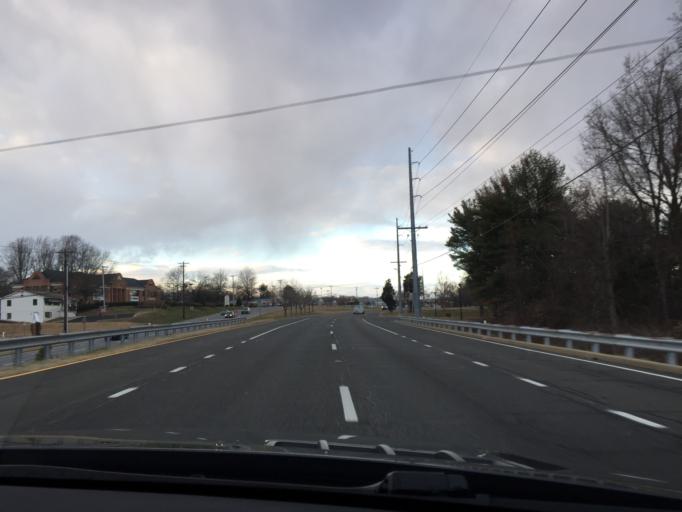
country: US
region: Maryland
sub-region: Calvert County
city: Dunkirk Town Center
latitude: 38.7136
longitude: -76.6573
